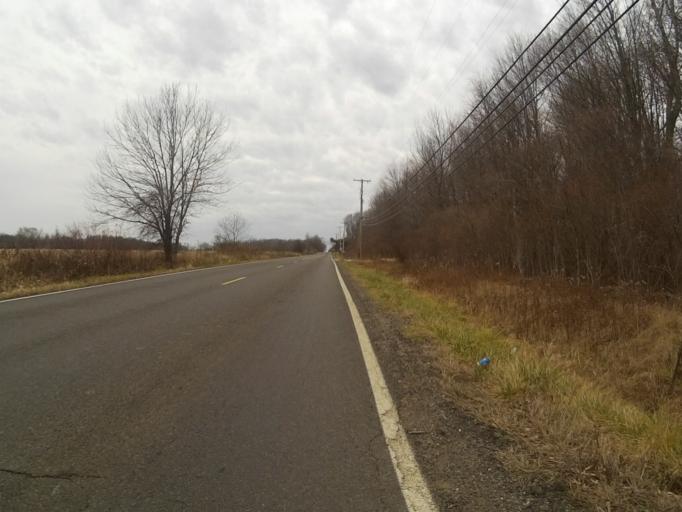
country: US
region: Ohio
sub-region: Portage County
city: Brimfield
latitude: 41.0828
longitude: -81.3335
